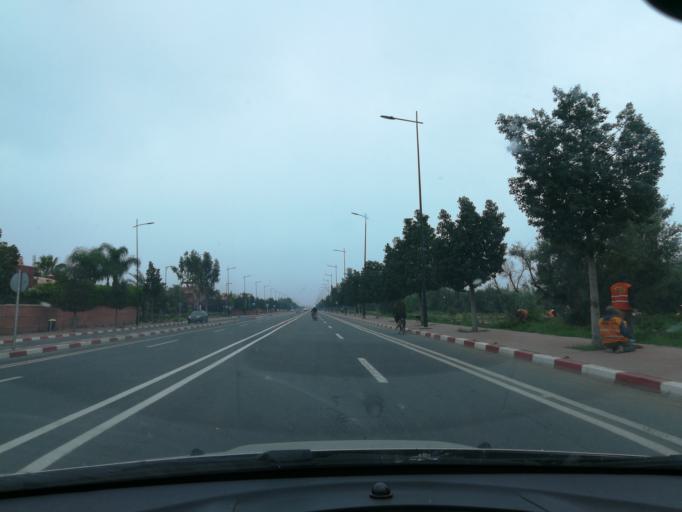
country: MA
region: Marrakech-Tensift-Al Haouz
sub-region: Marrakech
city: Marrakesh
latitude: 31.6142
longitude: -7.9964
